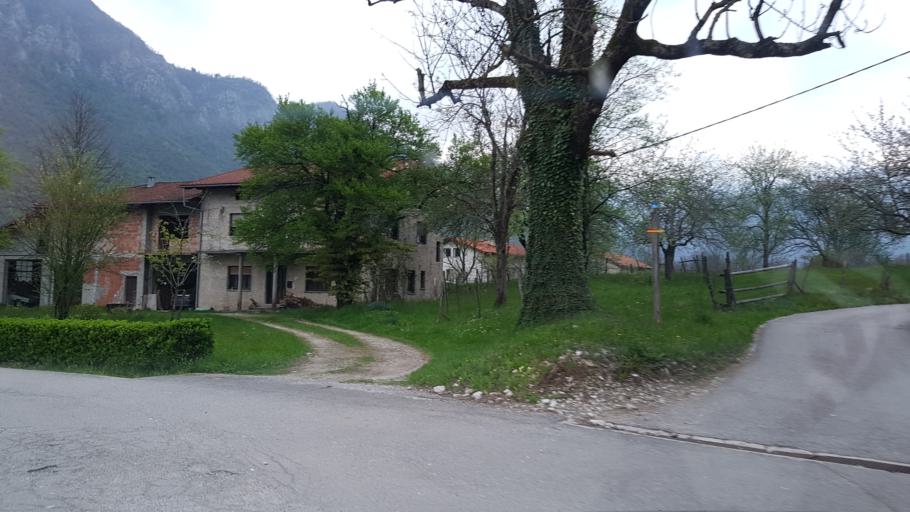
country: SI
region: Kobarid
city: Kobarid
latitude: 46.2430
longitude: 13.5528
